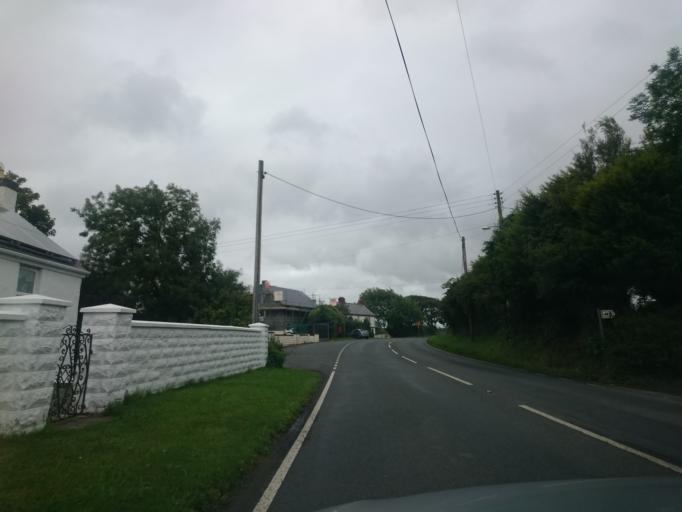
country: GB
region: Wales
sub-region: Pembrokeshire
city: Freystrop
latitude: 51.7743
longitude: -4.9652
